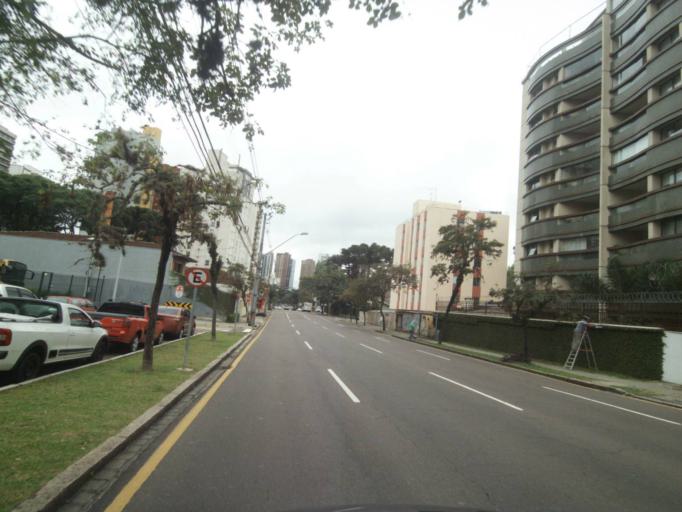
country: BR
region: Parana
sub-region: Curitiba
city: Curitiba
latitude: -25.4168
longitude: -49.2610
